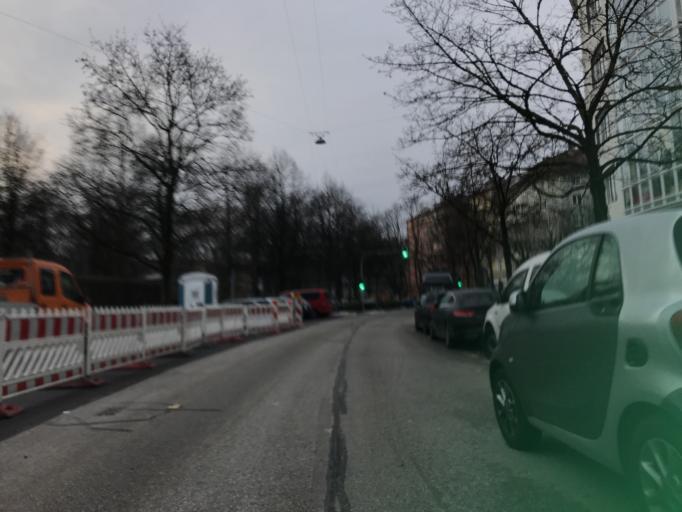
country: DE
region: Bavaria
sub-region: Upper Bavaria
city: Munich
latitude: 48.1548
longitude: 11.5683
